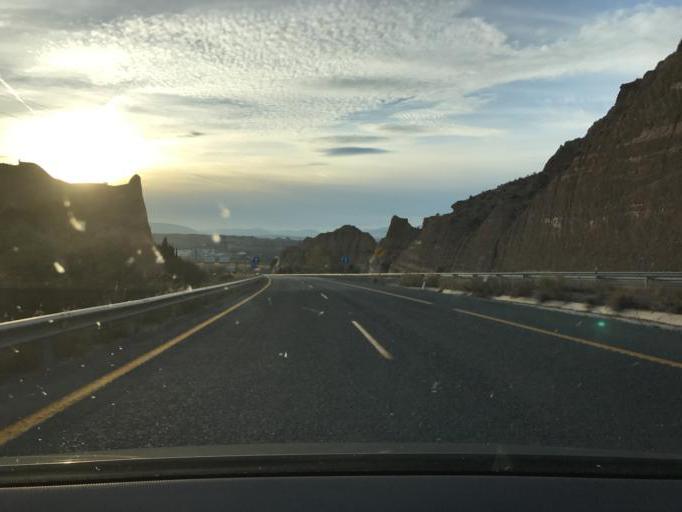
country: ES
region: Andalusia
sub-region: Provincia de Granada
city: Guadix
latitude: 37.3209
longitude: -3.1209
